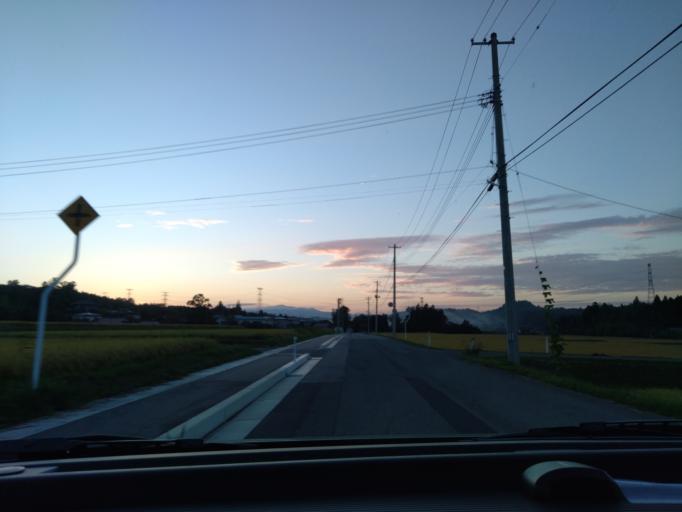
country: JP
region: Iwate
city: Ichinoseki
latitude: 38.8545
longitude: 141.1516
